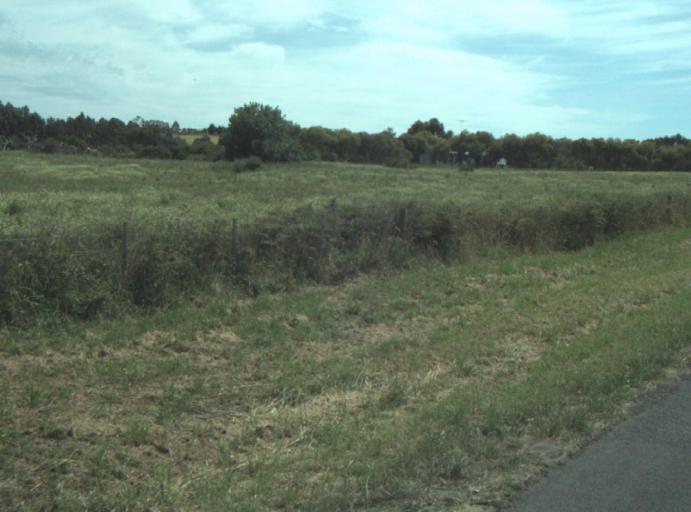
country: AU
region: Victoria
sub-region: Greater Geelong
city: Clifton Springs
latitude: -38.1563
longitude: 144.5873
